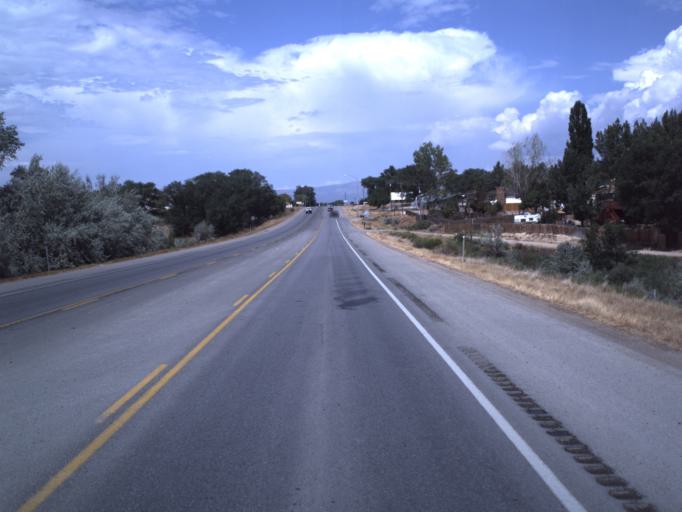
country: US
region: Utah
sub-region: Uintah County
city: Naples
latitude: 40.4101
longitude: -109.4892
